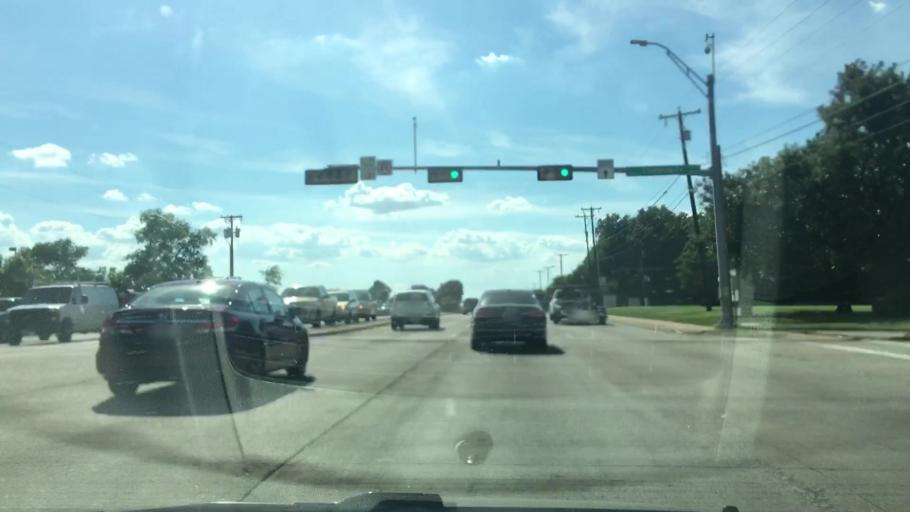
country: US
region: Texas
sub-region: Collin County
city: McKinney
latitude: 33.2170
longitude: -96.6440
